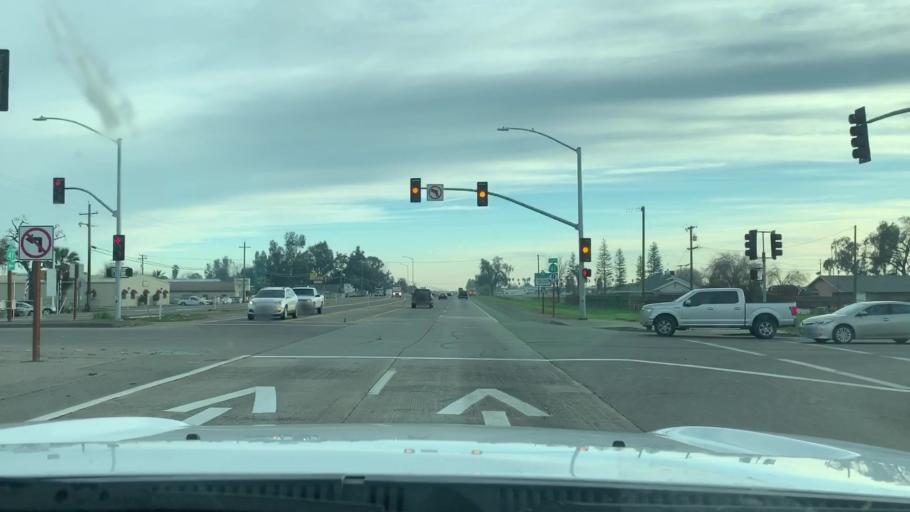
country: US
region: California
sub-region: Kings County
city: Lemoore
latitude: 36.3426
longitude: -119.8083
